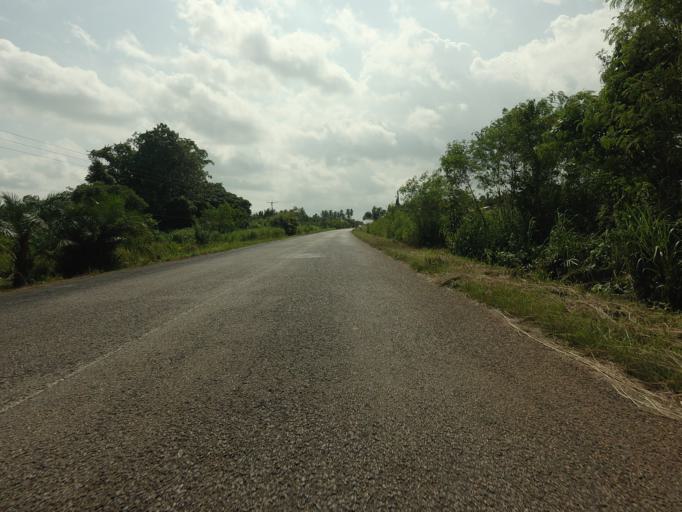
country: GH
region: Volta
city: Ho
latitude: 6.4118
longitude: 0.7604
